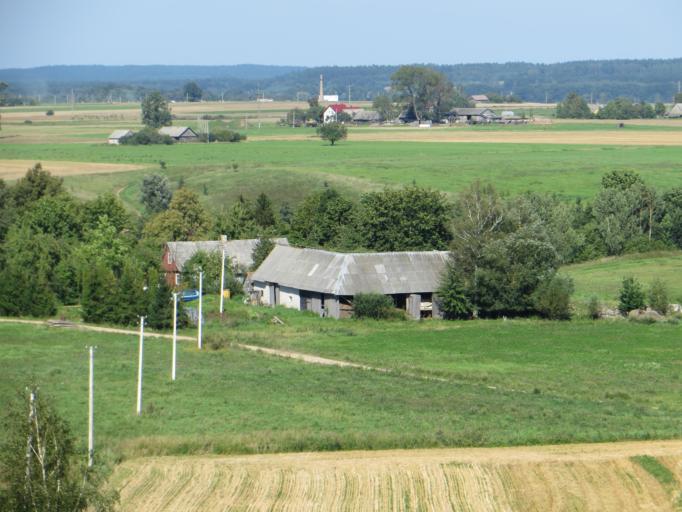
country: LT
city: Prienai
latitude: 54.4821
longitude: 23.8642
